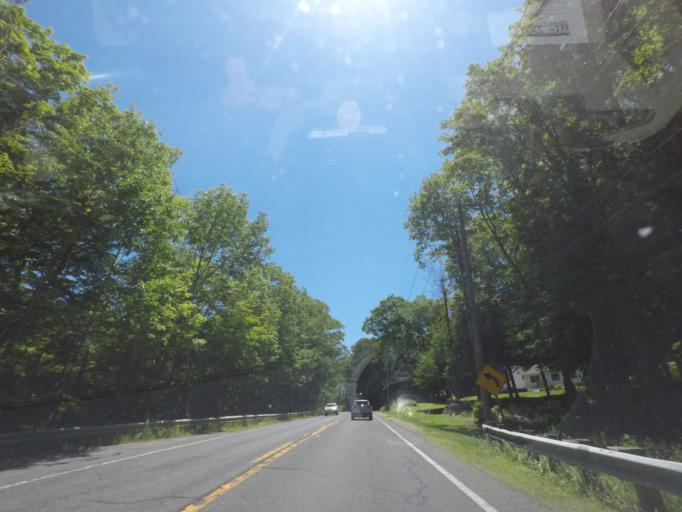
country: US
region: Massachusetts
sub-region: Berkshire County
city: Becket
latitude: 42.2722
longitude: -73.1415
